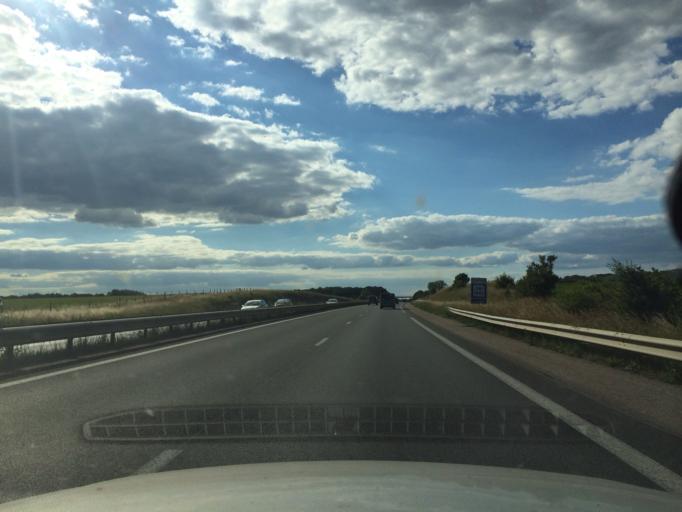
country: FR
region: Lorraine
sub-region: Departement de Meurthe-et-Moselle
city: Damelevieres
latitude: 48.5954
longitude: 6.3962
